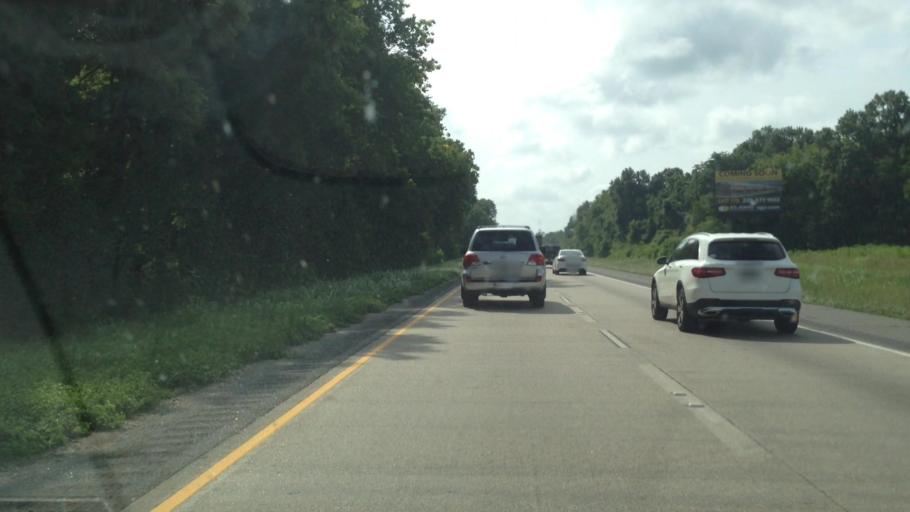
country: US
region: Louisiana
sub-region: Ascension Parish
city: Gonzales
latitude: 30.1877
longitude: -90.9113
